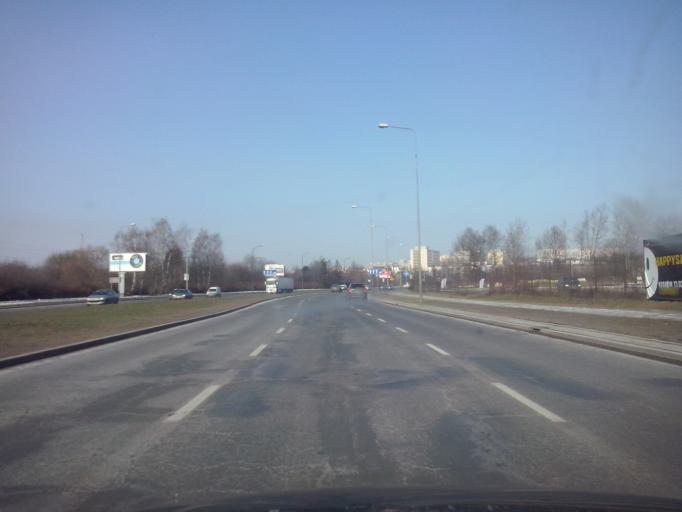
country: PL
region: Lesser Poland Voivodeship
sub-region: Krakow
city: Krakow
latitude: 50.0792
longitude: 20.0001
